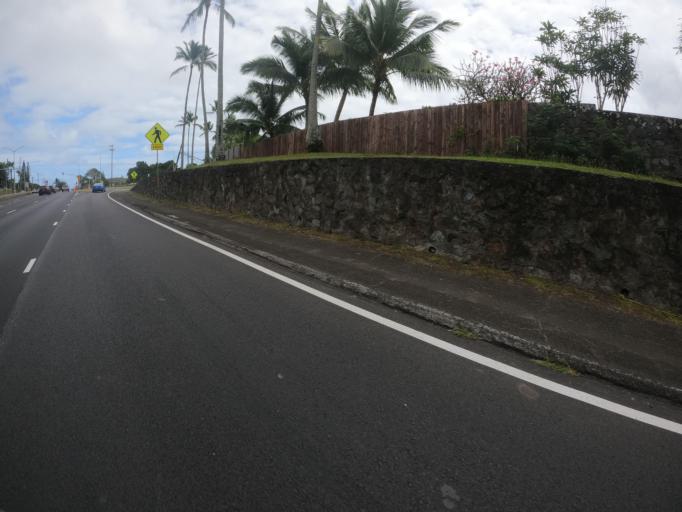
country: US
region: Hawaii
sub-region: Honolulu County
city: Maunawili
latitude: 21.3800
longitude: -157.7567
